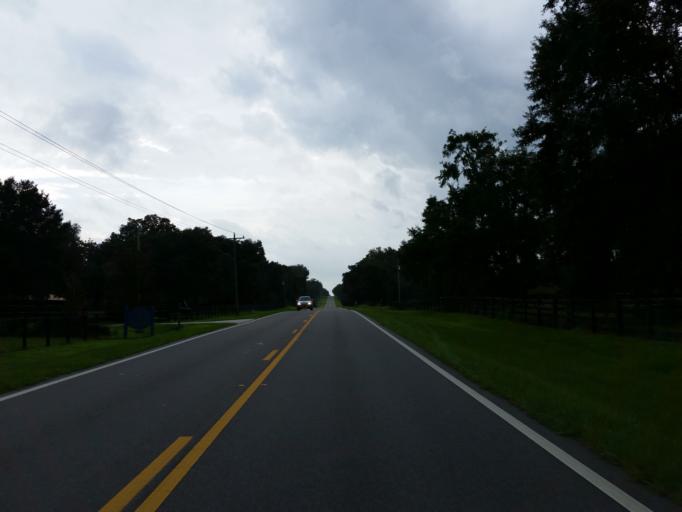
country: US
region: Florida
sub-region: Levy County
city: Williston
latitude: 29.4057
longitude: -82.3255
